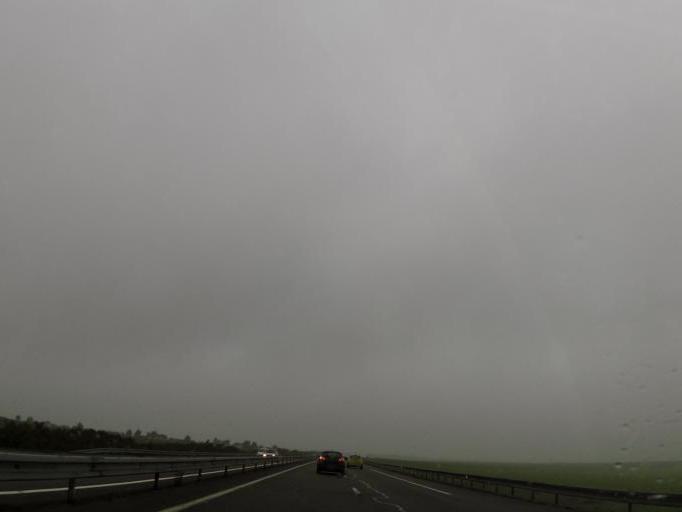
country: FR
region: Champagne-Ardenne
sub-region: Departement de la Marne
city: Courtisols
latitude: 49.0360
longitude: 4.6097
